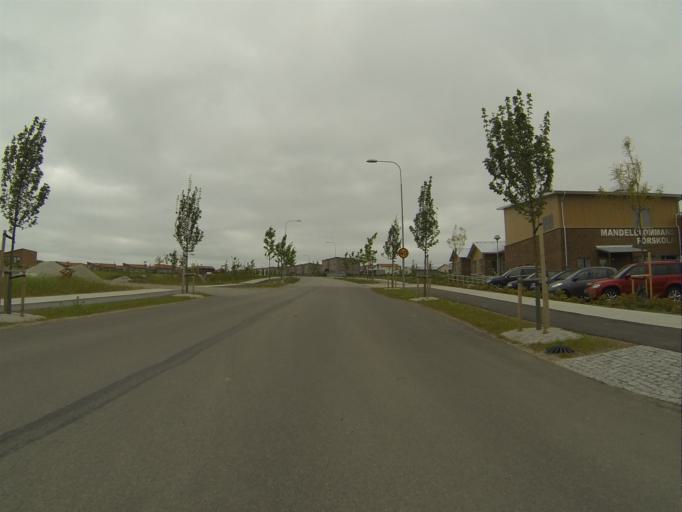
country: SE
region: Skane
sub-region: Lunds Kommun
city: Genarp
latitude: 55.6578
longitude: 13.3537
